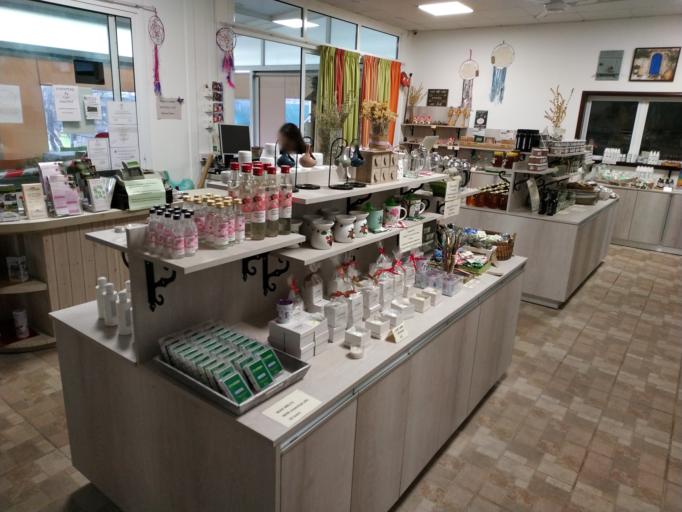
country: CY
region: Ammochostos
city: Avgorou
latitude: 35.0134
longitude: 33.8314
